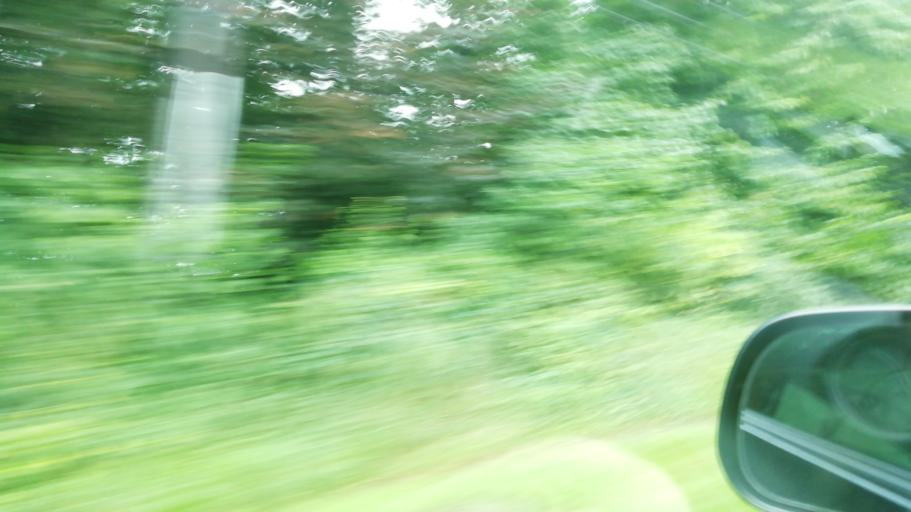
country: IE
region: Munster
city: Fethard
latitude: 52.5056
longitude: -7.6856
